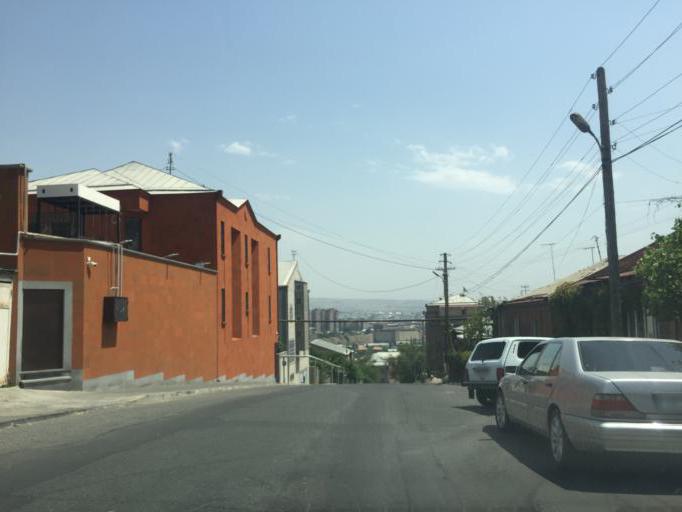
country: AM
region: Yerevan
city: Yerevan
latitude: 40.1754
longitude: 44.4917
